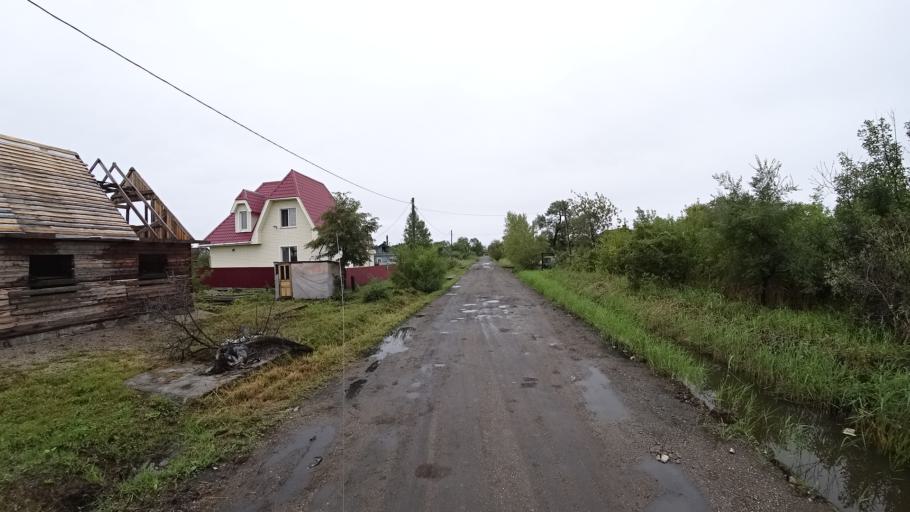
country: RU
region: Primorskiy
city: Monastyrishche
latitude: 44.2112
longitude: 132.4337
